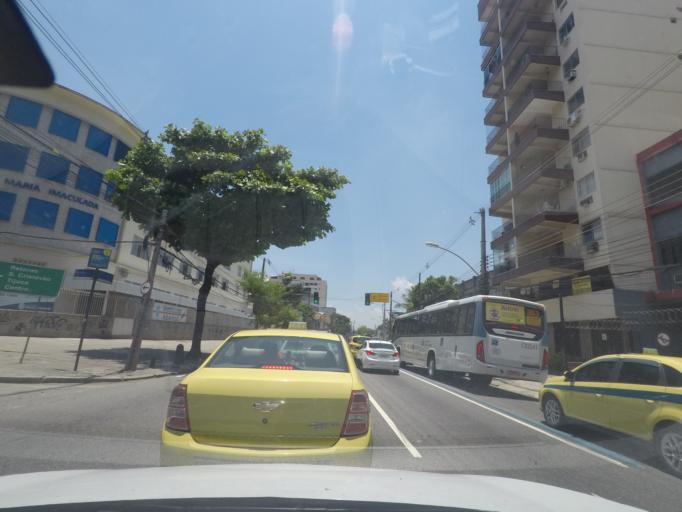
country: BR
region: Rio de Janeiro
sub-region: Rio De Janeiro
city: Rio de Janeiro
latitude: -22.9044
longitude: -43.2431
